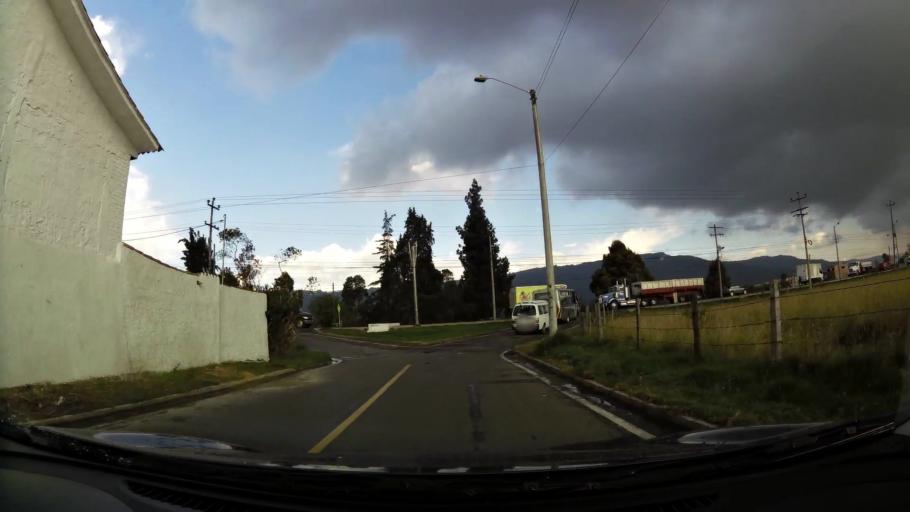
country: CO
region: Cundinamarca
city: Chia
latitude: 4.8601
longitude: -74.0478
